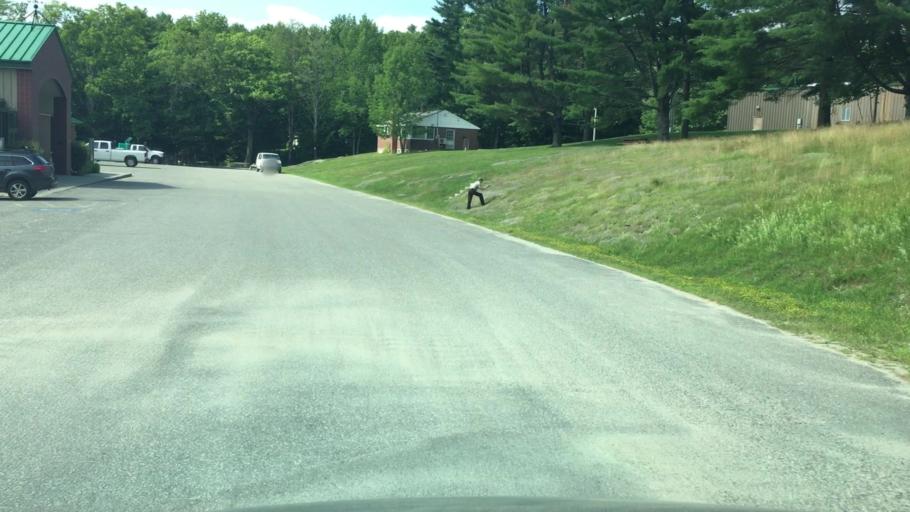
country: US
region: Maine
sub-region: Hancock County
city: Orland
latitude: 44.5849
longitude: -68.6885
